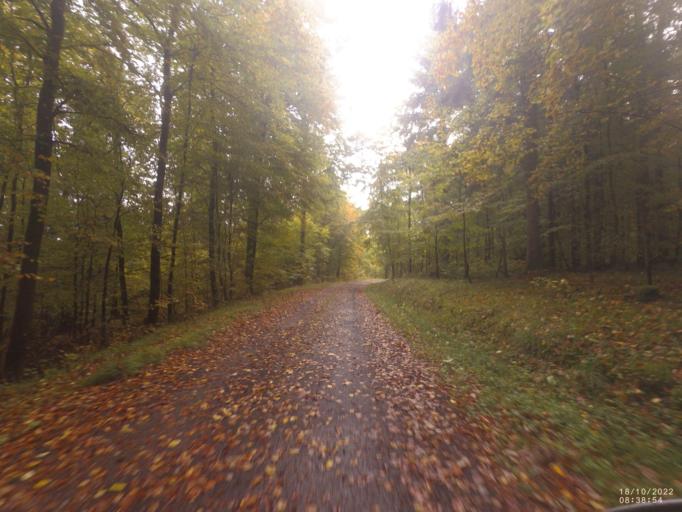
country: DE
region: Rheinland-Pfalz
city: Daun
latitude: 50.2254
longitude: 6.8191
